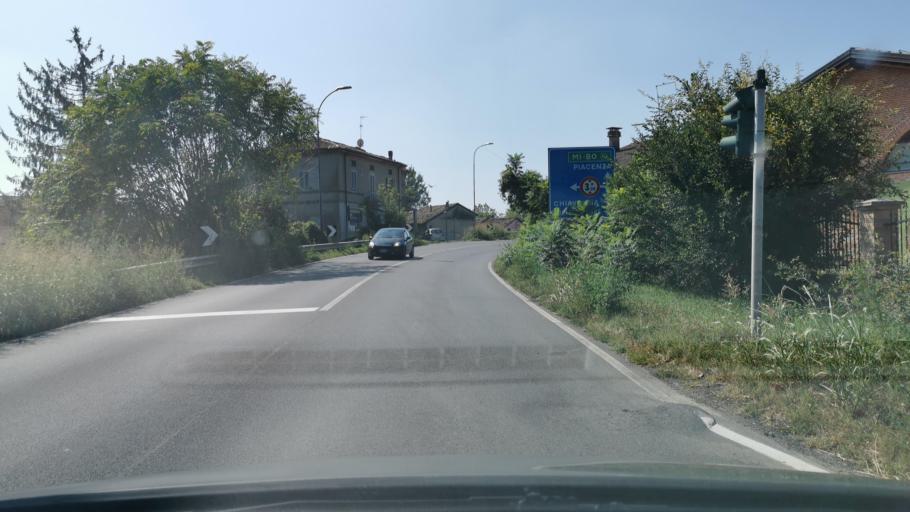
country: IT
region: Emilia-Romagna
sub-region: Provincia di Piacenza
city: Caorso
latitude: 45.0490
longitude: 9.8774
